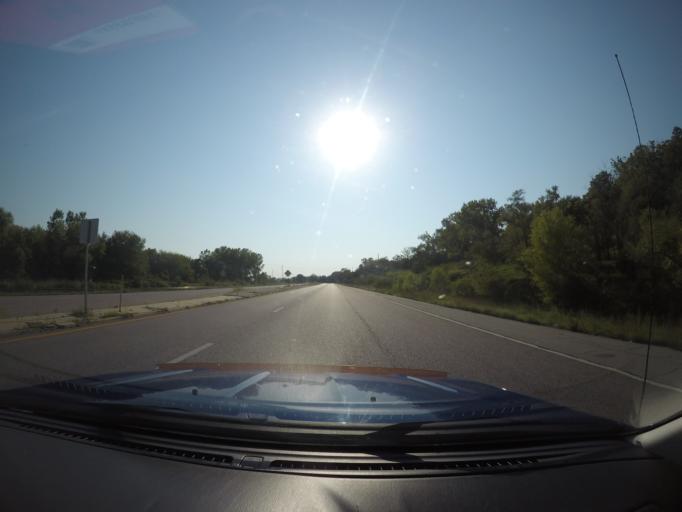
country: US
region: Kansas
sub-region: Wyandotte County
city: Edwardsville
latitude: 39.0615
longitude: -94.7960
